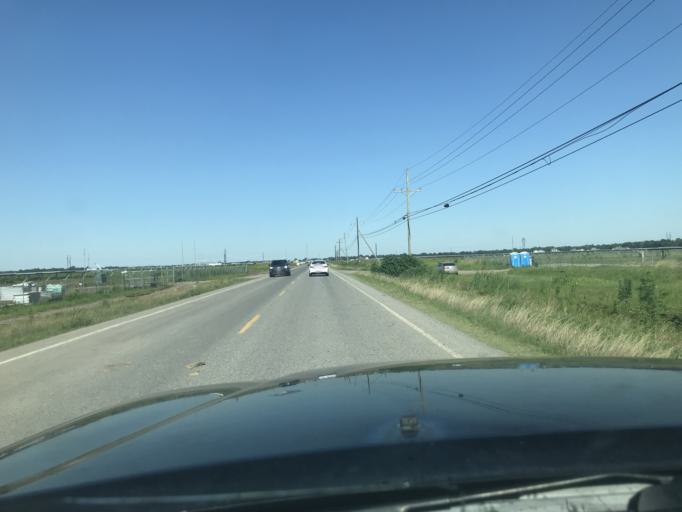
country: US
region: Louisiana
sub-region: West Baton Rouge Parish
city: Brusly
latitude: 30.4688
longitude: -91.3207
